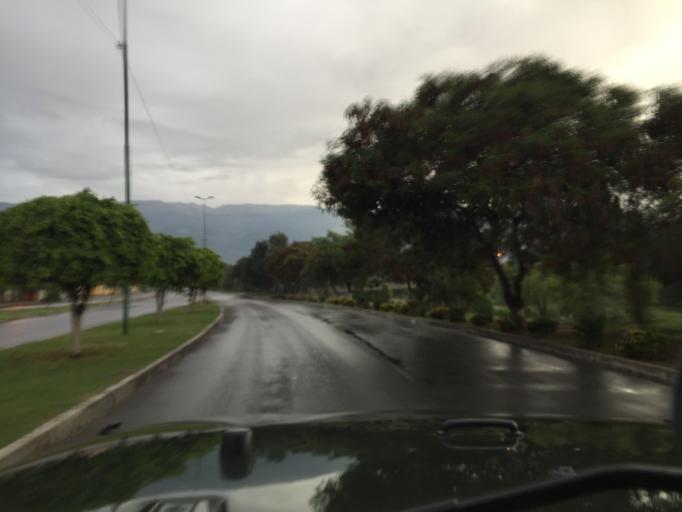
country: BO
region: Cochabamba
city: Cochabamba
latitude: -17.4029
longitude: -66.1695
